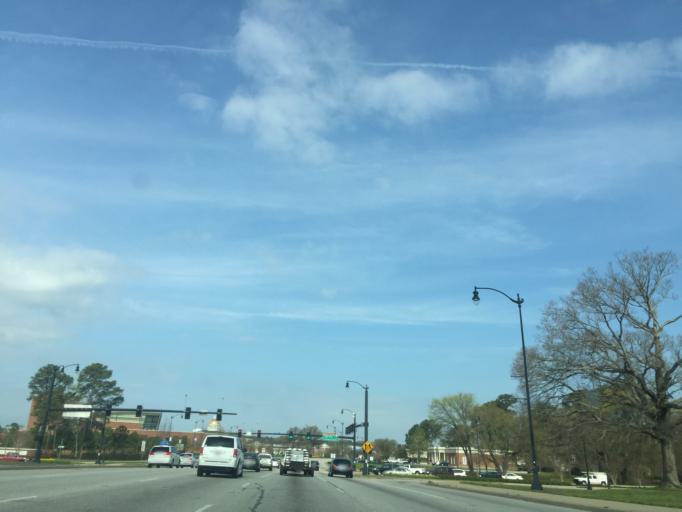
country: US
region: Virginia
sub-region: City of Newport News
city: Newport News
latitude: 37.0611
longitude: -76.4860
